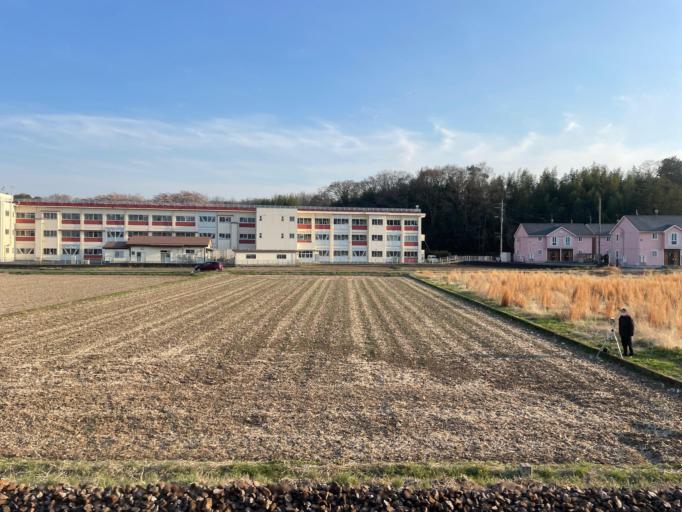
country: JP
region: Gunma
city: Annaka
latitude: 36.3320
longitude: 138.9264
